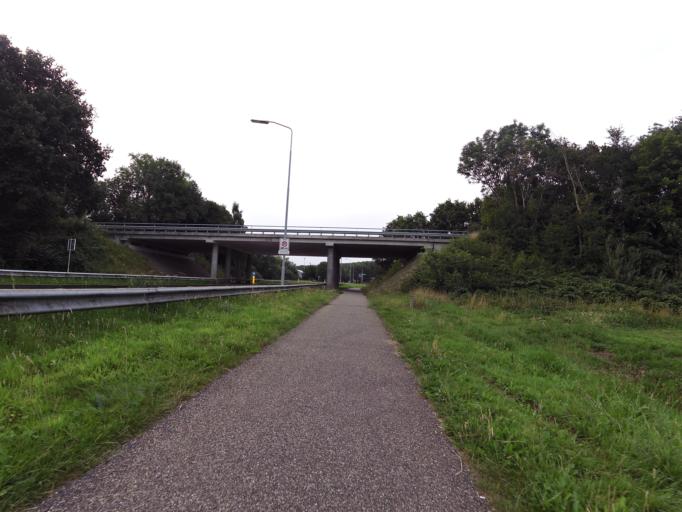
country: NL
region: Gelderland
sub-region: Gemeente Doesburg
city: Doesburg
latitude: 51.9985
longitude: 6.1410
